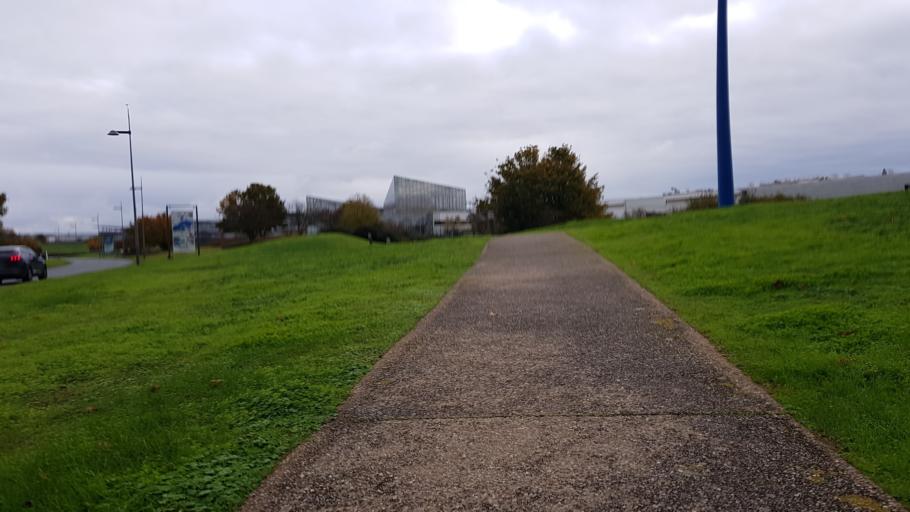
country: FR
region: Poitou-Charentes
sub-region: Departement de la Vienne
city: Chasseneuil-du-Poitou
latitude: 46.6624
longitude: 0.3621
